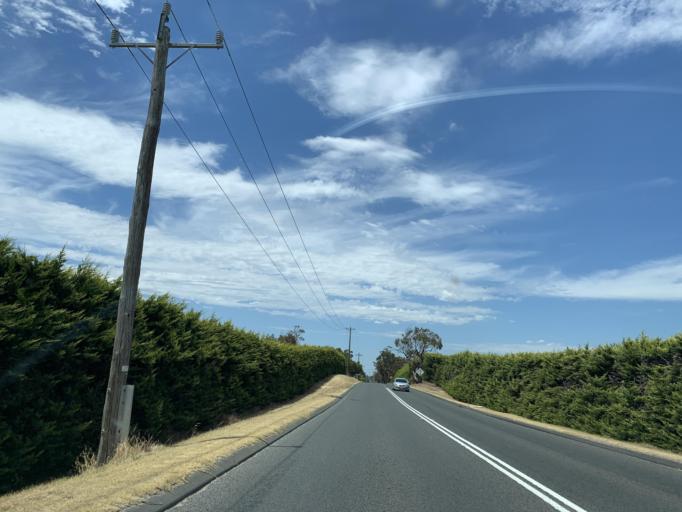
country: AU
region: Victoria
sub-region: Mornington Peninsula
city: Tyabb
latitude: -38.2386
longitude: 145.2093
